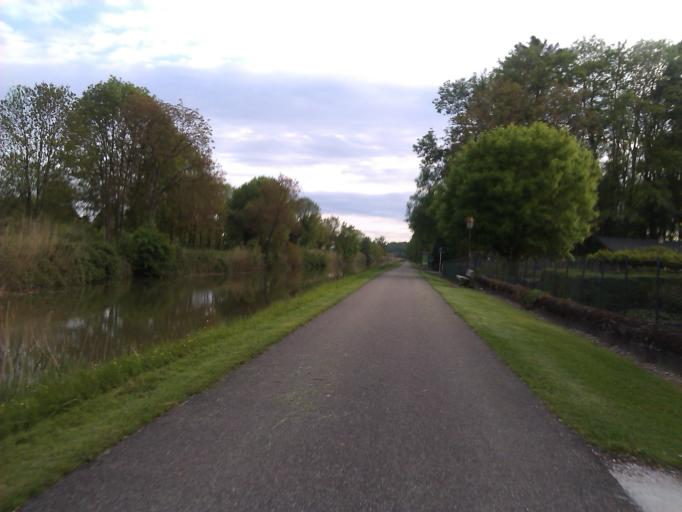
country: FR
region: Franche-Comte
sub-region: Departement du Jura
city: Dole
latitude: 47.1233
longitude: 5.5619
